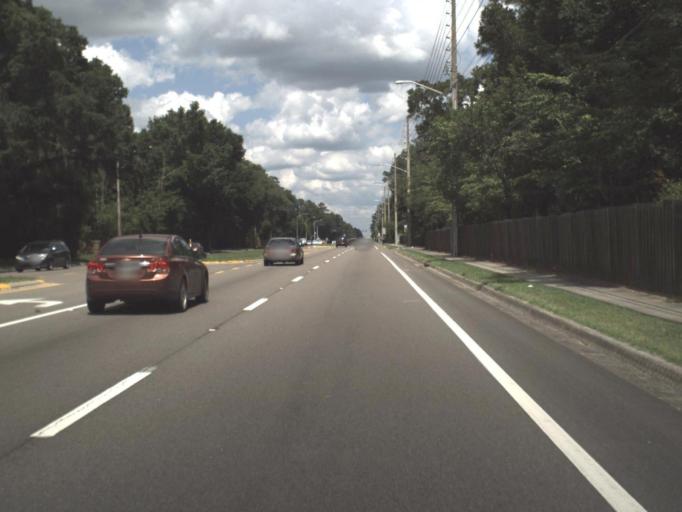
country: US
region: Florida
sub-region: Alachua County
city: Gainesville
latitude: 29.6886
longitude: -82.3777
